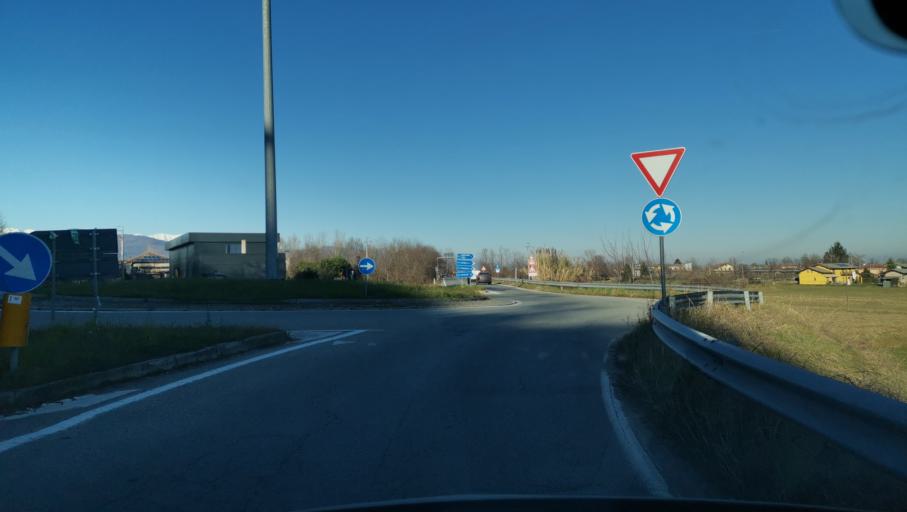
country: IT
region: Piedmont
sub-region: Provincia di Torino
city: Bibiana
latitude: 44.7890
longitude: 7.2933
